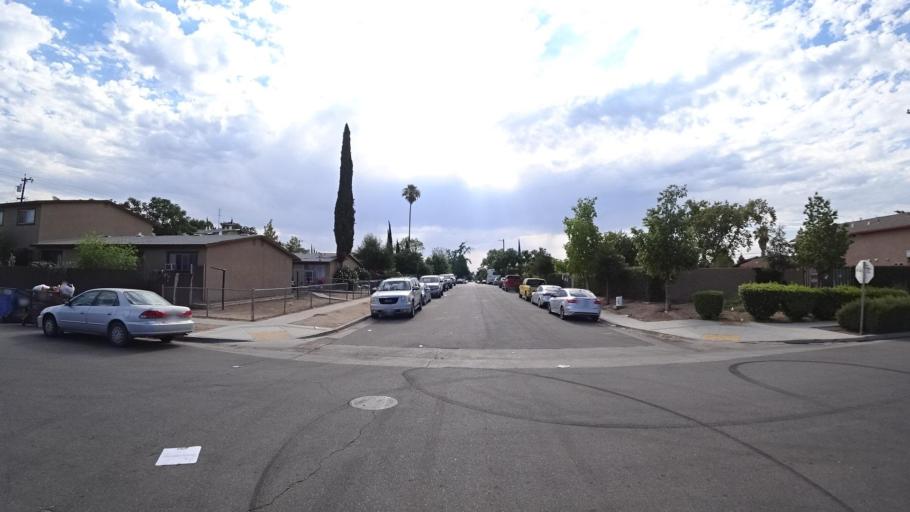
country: US
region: California
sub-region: Fresno County
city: Fresno
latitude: 36.7568
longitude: -119.7680
